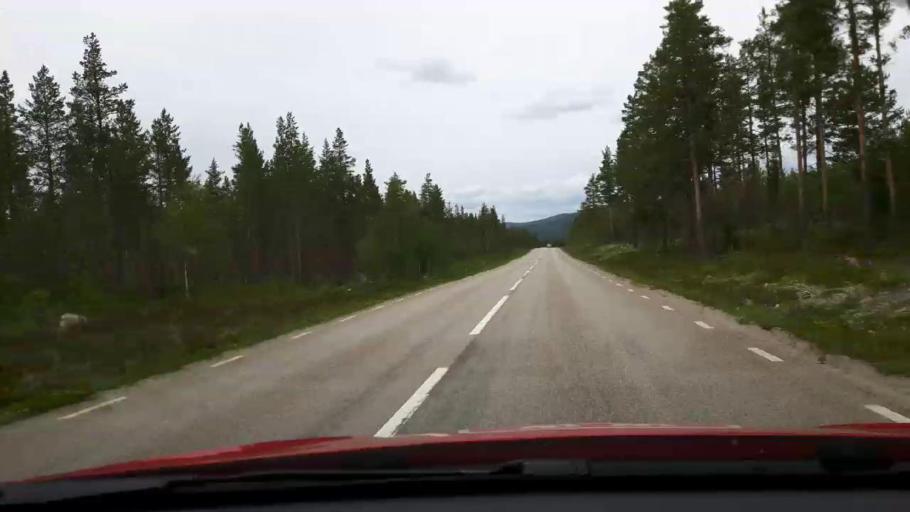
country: SE
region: Jaemtland
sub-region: Harjedalens Kommun
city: Sveg
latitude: 62.2530
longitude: 13.8411
